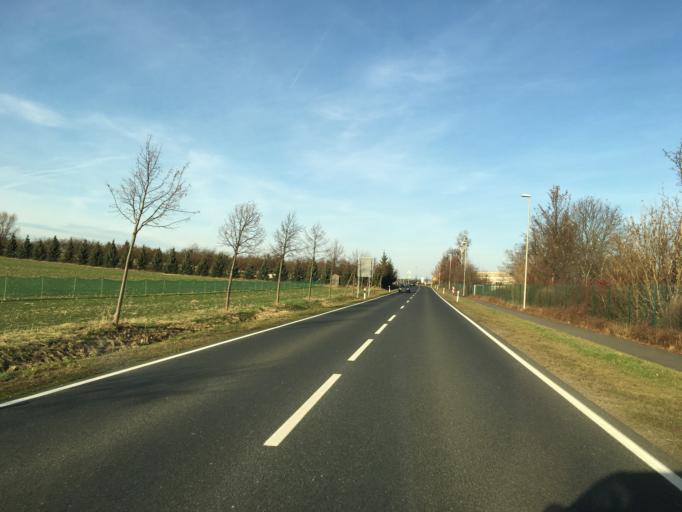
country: DE
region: Saxony
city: Oschatz
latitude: 51.2866
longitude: 13.1263
